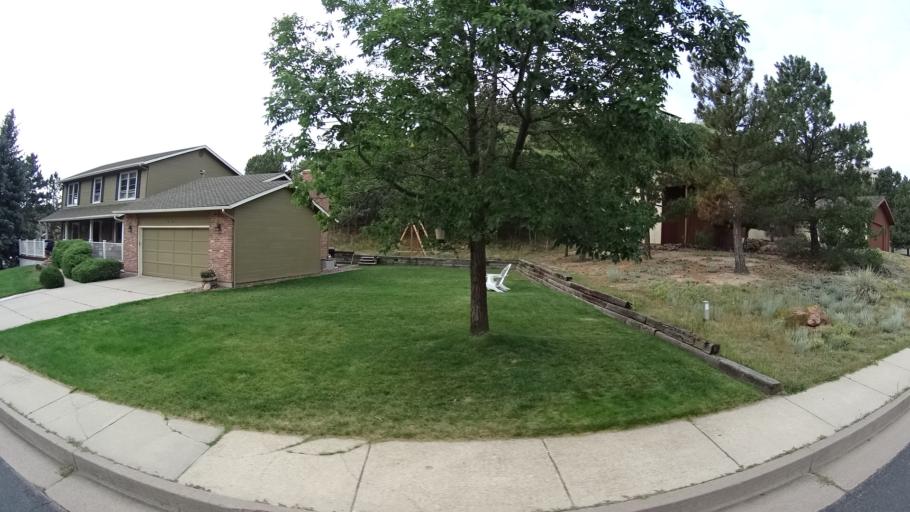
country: US
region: Colorado
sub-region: El Paso County
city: Air Force Academy
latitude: 38.9322
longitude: -104.8568
